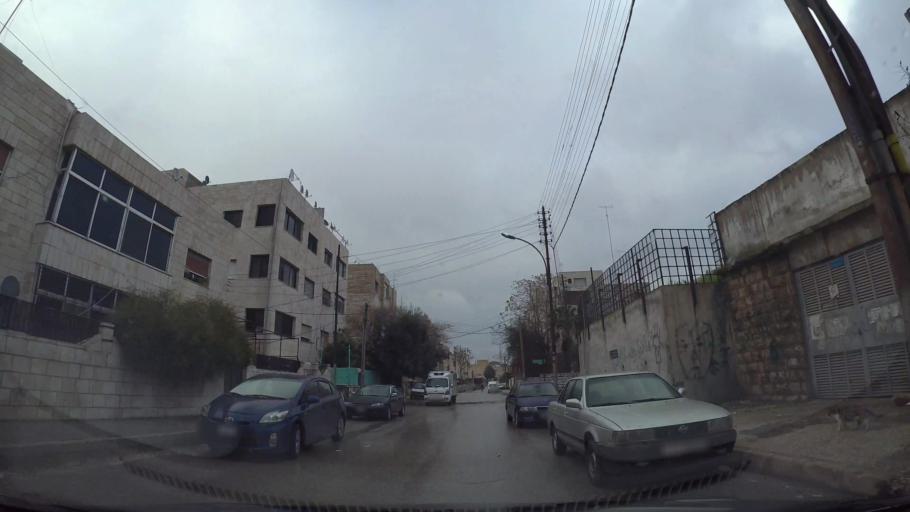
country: JO
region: Amman
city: Amman
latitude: 31.9680
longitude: 35.9221
